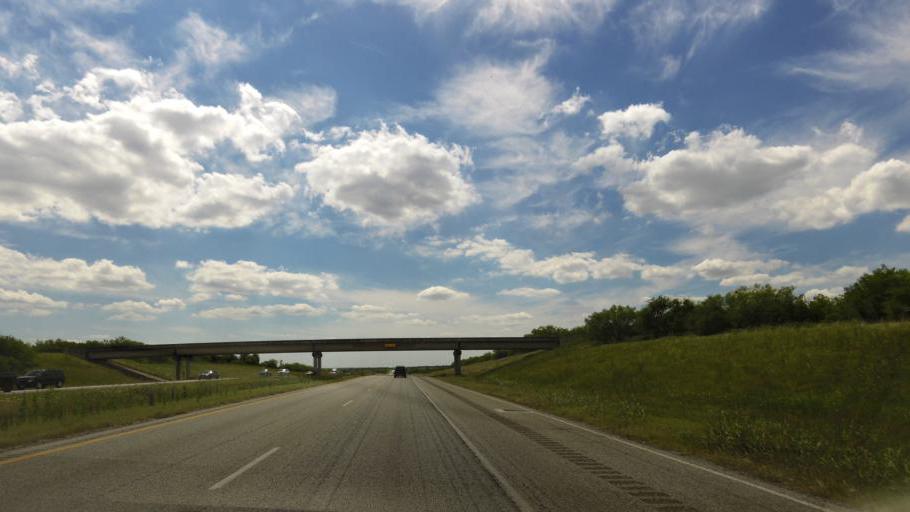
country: US
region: Texas
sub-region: Gonzales County
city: Waelder
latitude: 29.6669
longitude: -97.3325
